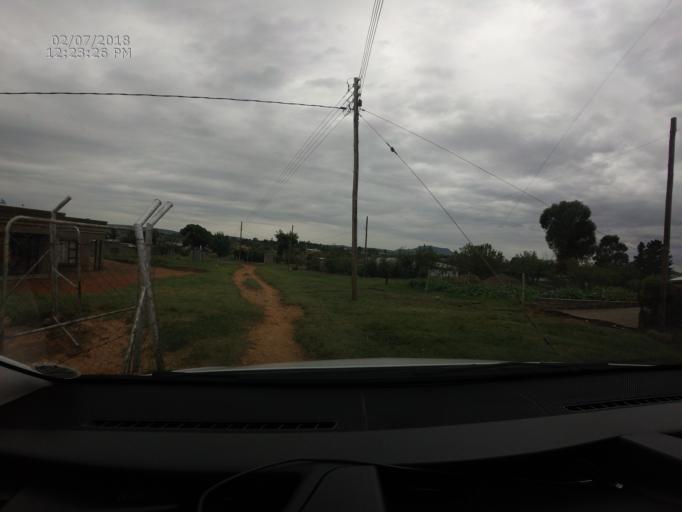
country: LS
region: Berea
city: Teyateyaneng
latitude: -29.1190
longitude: 27.9600
